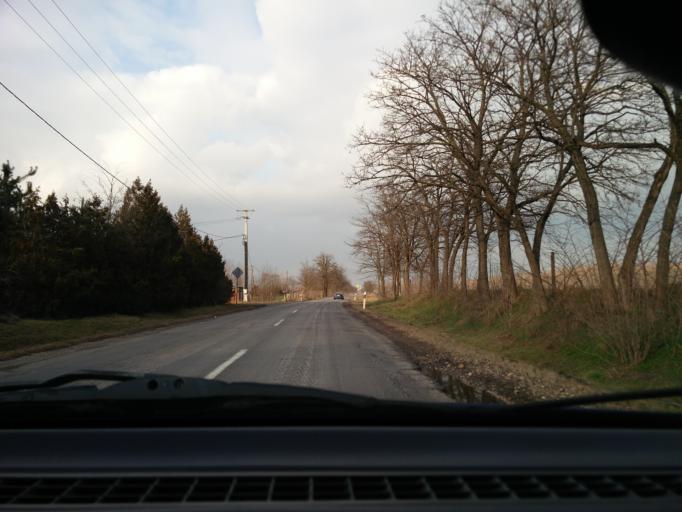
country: HU
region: Pest
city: Tapioszolos
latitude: 47.2938
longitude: 19.8679
